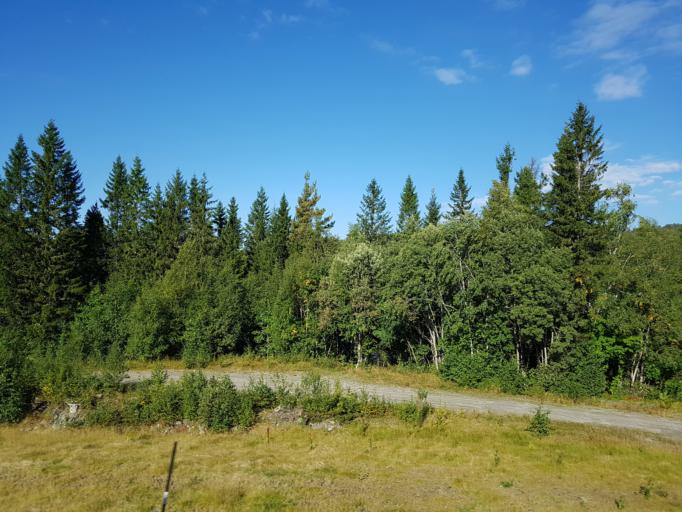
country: NO
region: Sor-Trondelag
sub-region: Trondheim
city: Trondheim
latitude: 63.6328
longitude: 10.2656
